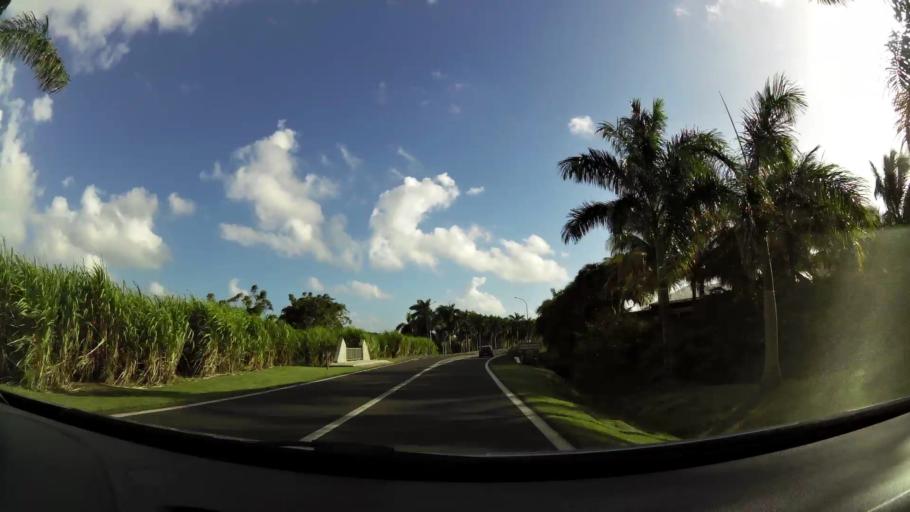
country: MQ
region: Martinique
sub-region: Martinique
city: Le Francois
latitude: 14.6152
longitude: -60.9115
